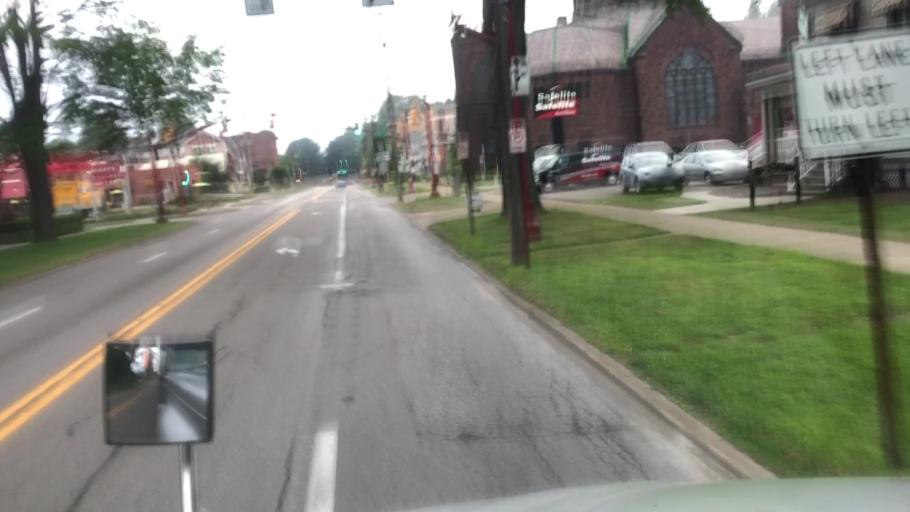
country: US
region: Pennsylvania
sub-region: Venango County
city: Franklin
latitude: 41.3944
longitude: -79.8261
